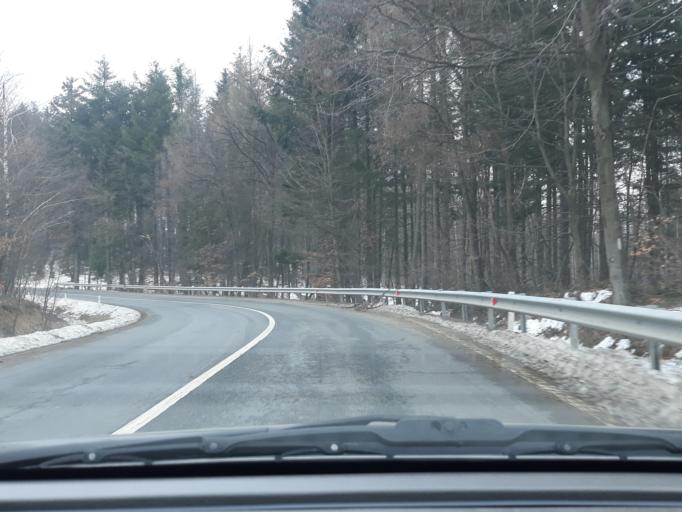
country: RO
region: Bihor
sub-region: Comuna Sinteu
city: Sinteu
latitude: 47.1210
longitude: 22.4404
